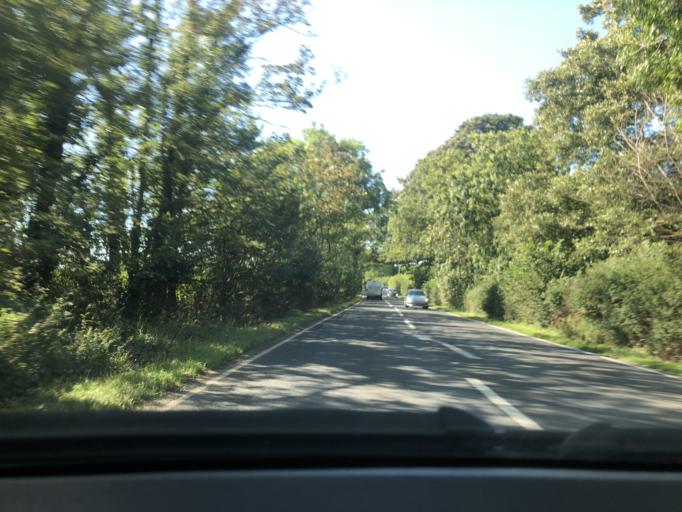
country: GB
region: England
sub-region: Somerset
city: Woolavington
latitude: 51.1547
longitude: -2.9274
